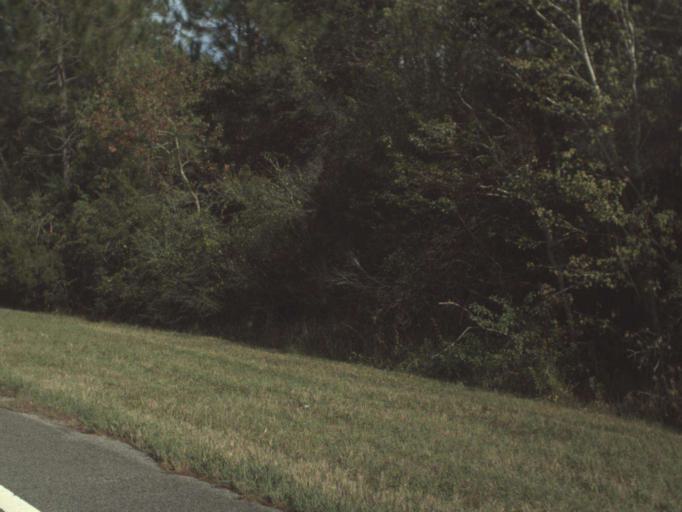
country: US
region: Florida
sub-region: Escambia County
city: Myrtle Grove
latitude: 30.3507
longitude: -87.3536
